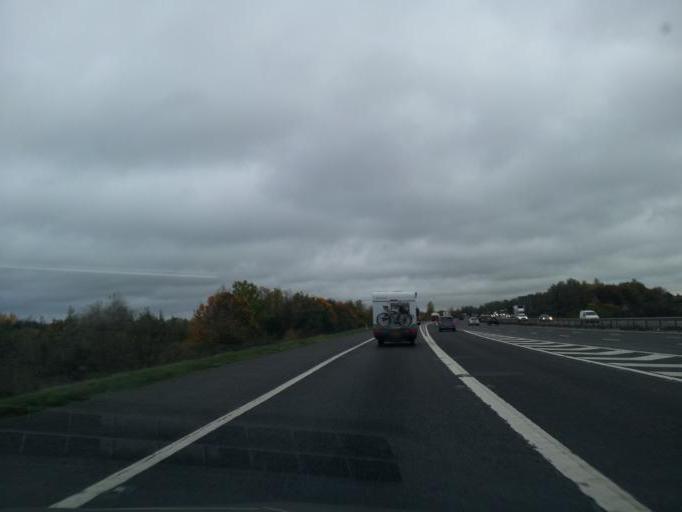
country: GB
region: England
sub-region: Oxfordshire
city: Bicester
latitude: 51.8726
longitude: -1.2008
